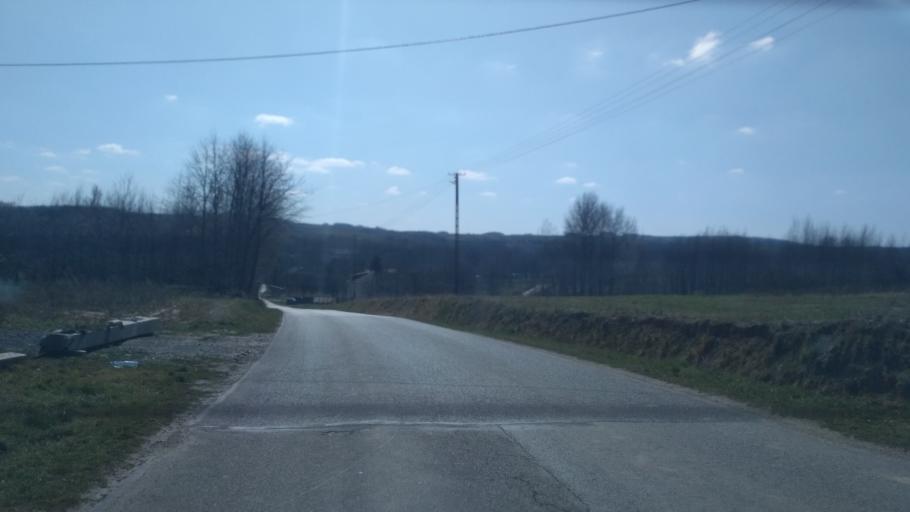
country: PL
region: Subcarpathian Voivodeship
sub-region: Powiat przeworski
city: Pantalowice
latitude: 49.9315
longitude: 22.4418
